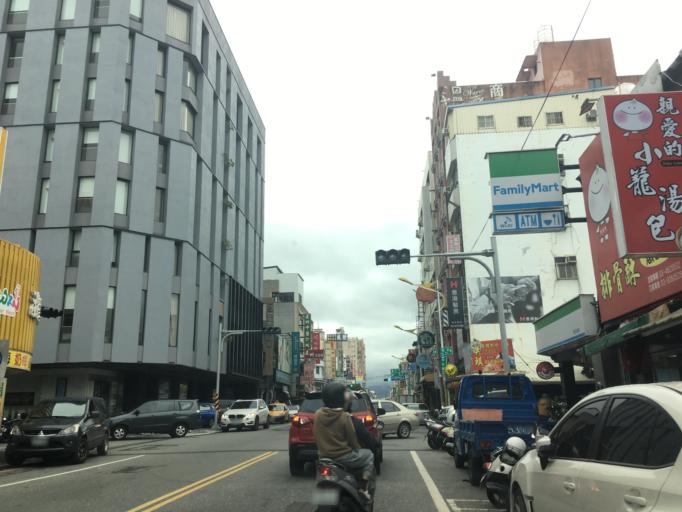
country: TW
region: Taiwan
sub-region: Hualien
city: Hualian
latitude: 23.9751
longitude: 121.6040
